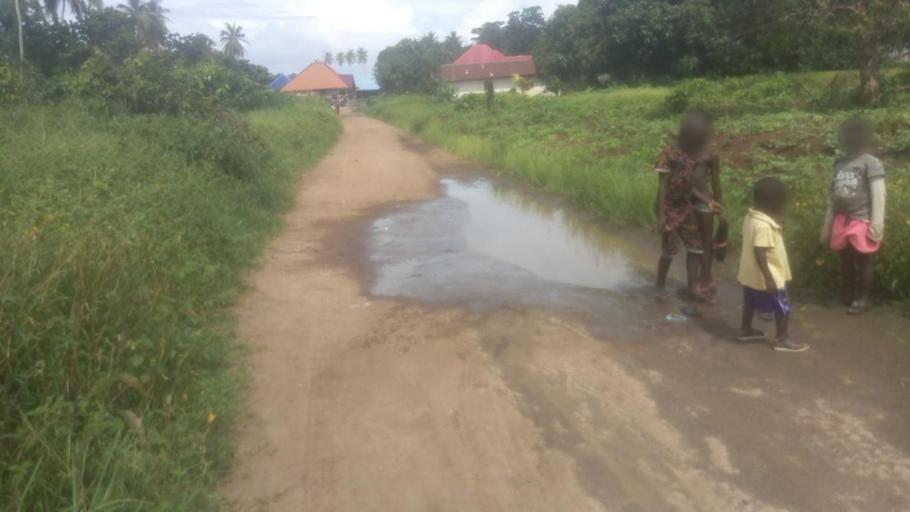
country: SL
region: Northern Province
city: Masoyila
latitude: 8.5890
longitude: -13.1961
